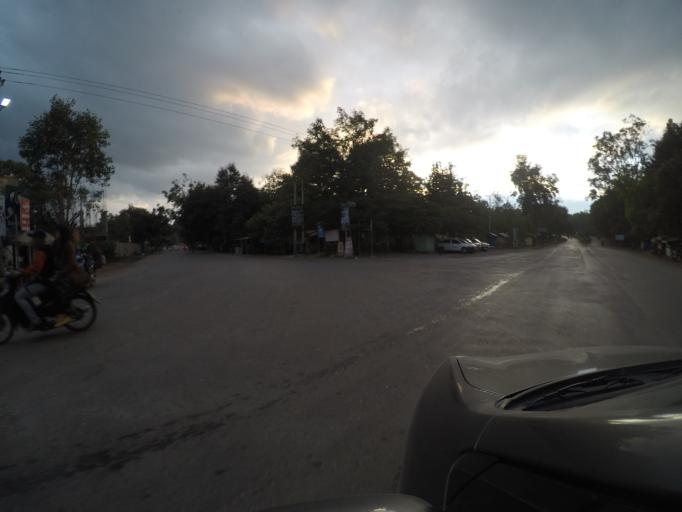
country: MM
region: Shan
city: Taunggyi
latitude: 20.7884
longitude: 96.9975
